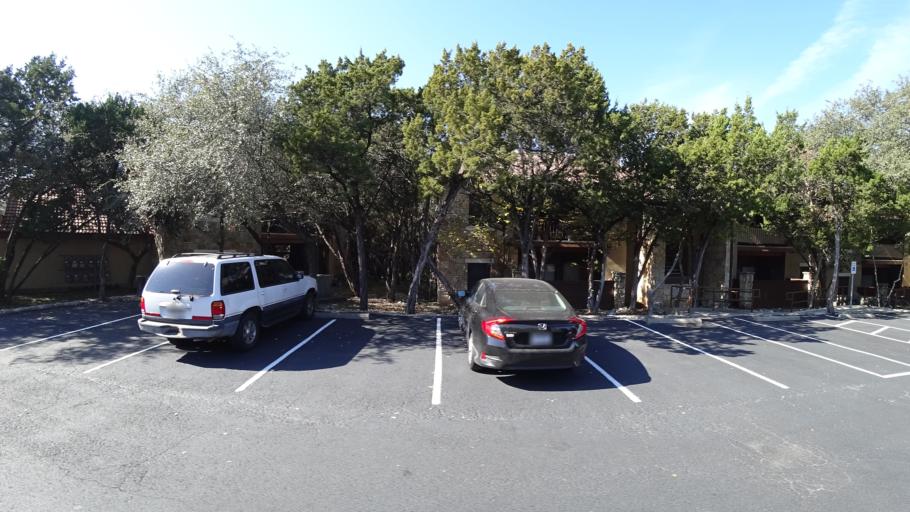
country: US
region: Texas
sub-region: Williamson County
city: Jollyville
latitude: 30.3743
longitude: -97.7617
